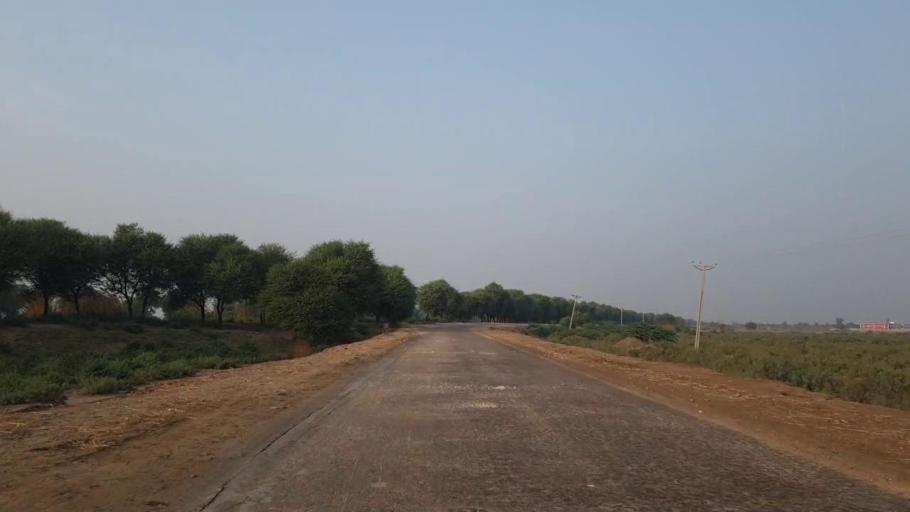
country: PK
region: Sindh
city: Tando Muhammad Khan
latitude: 25.1184
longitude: 68.4283
